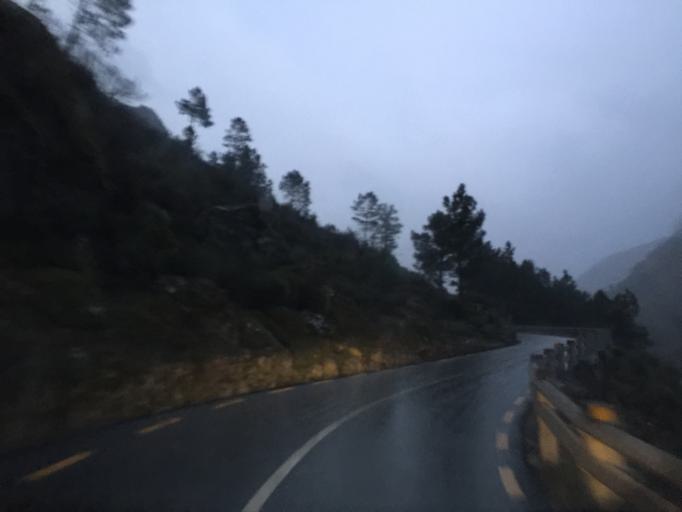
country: PT
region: Guarda
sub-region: Manteigas
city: Manteigas
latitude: 40.3653
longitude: -7.5527
